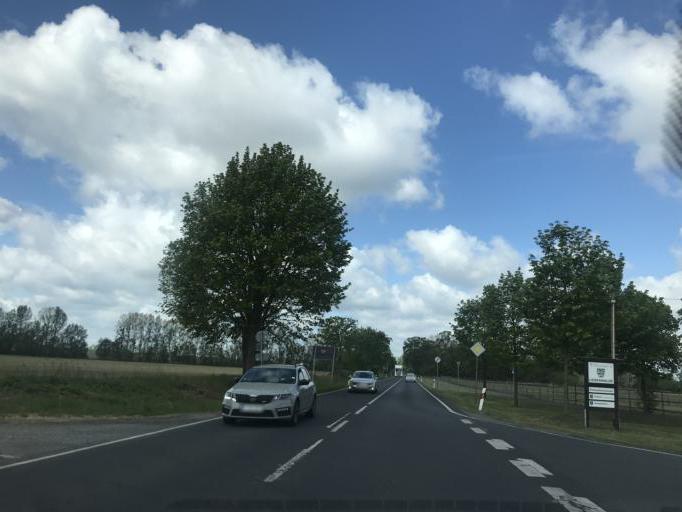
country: DE
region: Brandenburg
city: Liebenwalde
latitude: 52.8744
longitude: 13.4329
